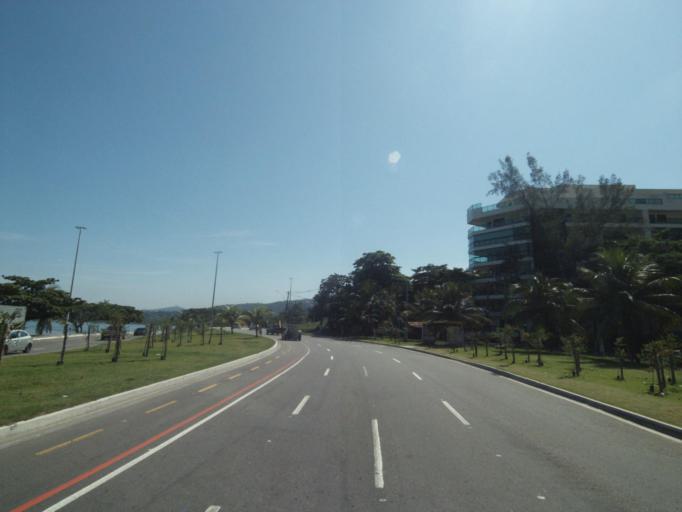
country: BR
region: Rio de Janeiro
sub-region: Niteroi
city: Niteroi
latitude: -22.9312
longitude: -43.0977
